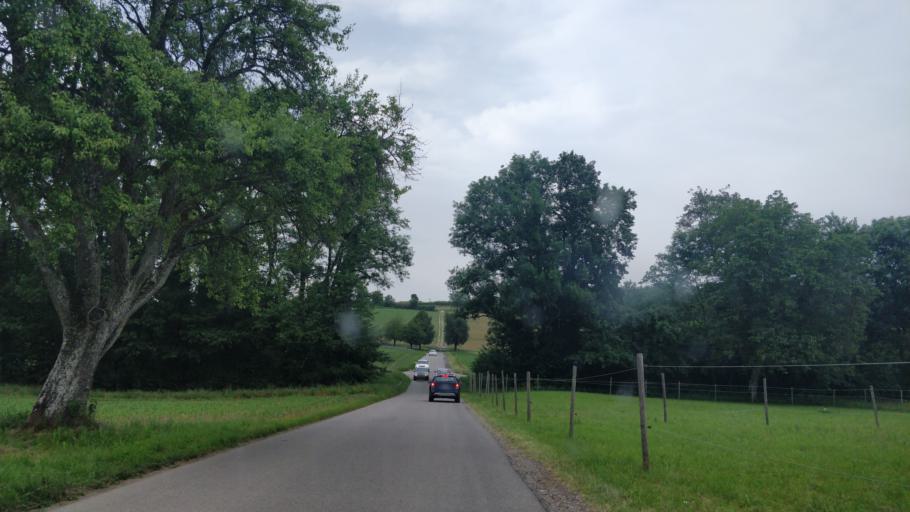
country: DE
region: Baden-Wuerttemberg
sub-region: Freiburg Region
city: Lottstetten
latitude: 47.6351
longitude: 8.5746
